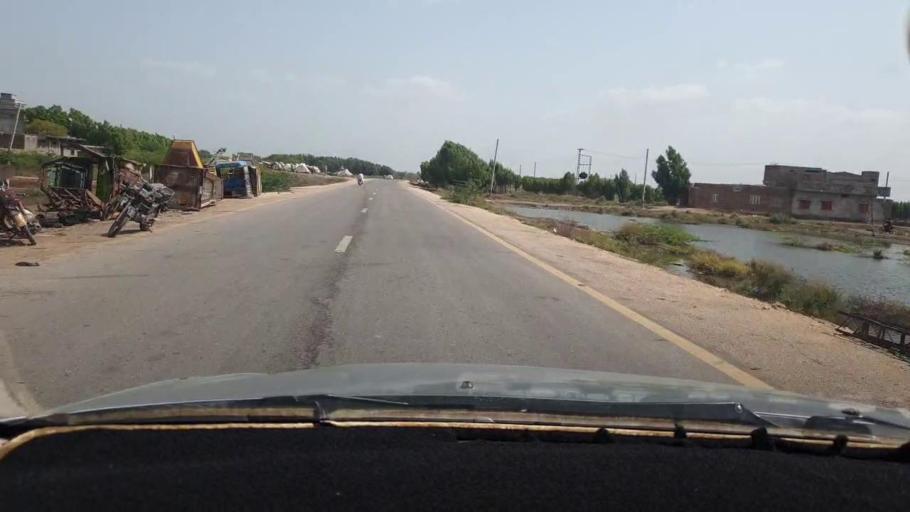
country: PK
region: Sindh
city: Digri
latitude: 25.1586
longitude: 69.1198
